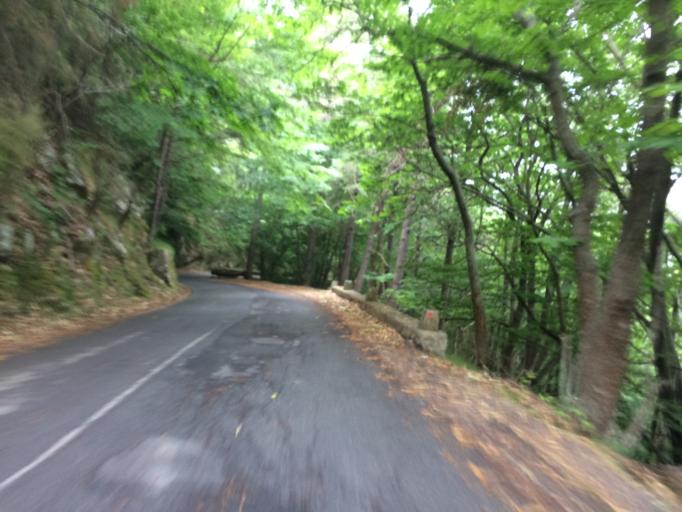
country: IT
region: Liguria
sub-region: Provincia di Imperia
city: Ceriana
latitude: 43.8749
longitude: 7.7467
